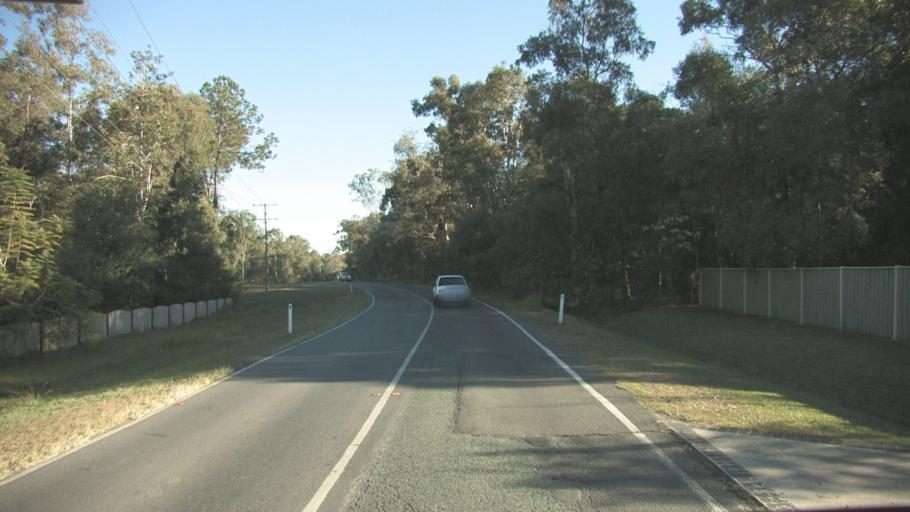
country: AU
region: Queensland
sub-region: Logan
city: Chambers Flat
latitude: -27.7548
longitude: 153.0502
